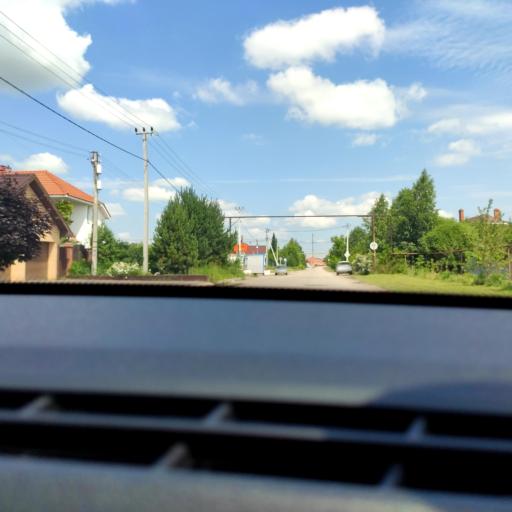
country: RU
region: Samara
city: Podstepki
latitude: 53.5700
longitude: 49.0802
